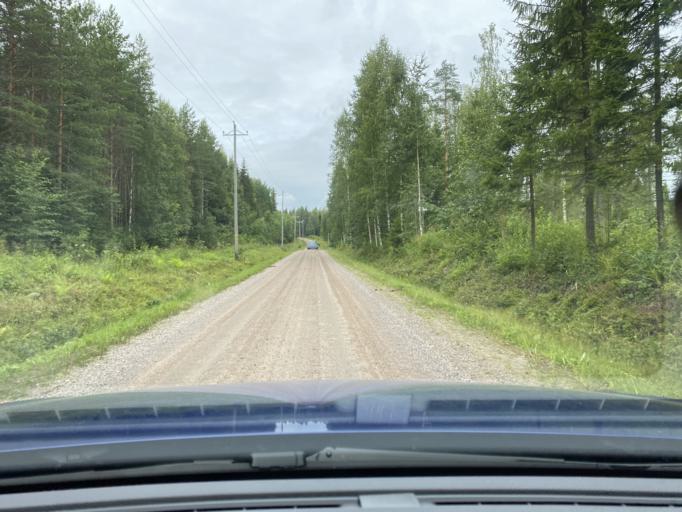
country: FI
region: Pirkanmaa
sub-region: Ylae-Pirkanmaa
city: Maenttae
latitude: 62.0203
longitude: 24.7355
